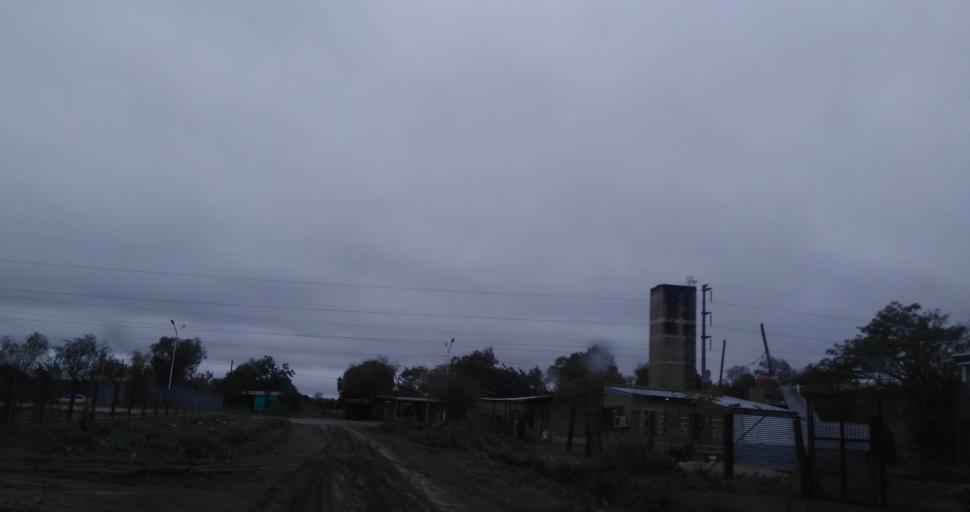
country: AR
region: Chaco
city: Fontana
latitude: -27.4221
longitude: -59.0207
